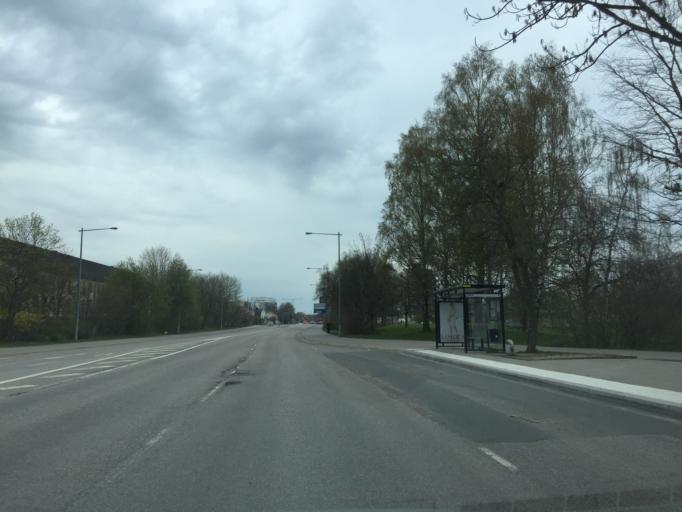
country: SE
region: OErebro
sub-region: Orebro Kommun
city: Orebro
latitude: 59.2597
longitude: 15.2406
